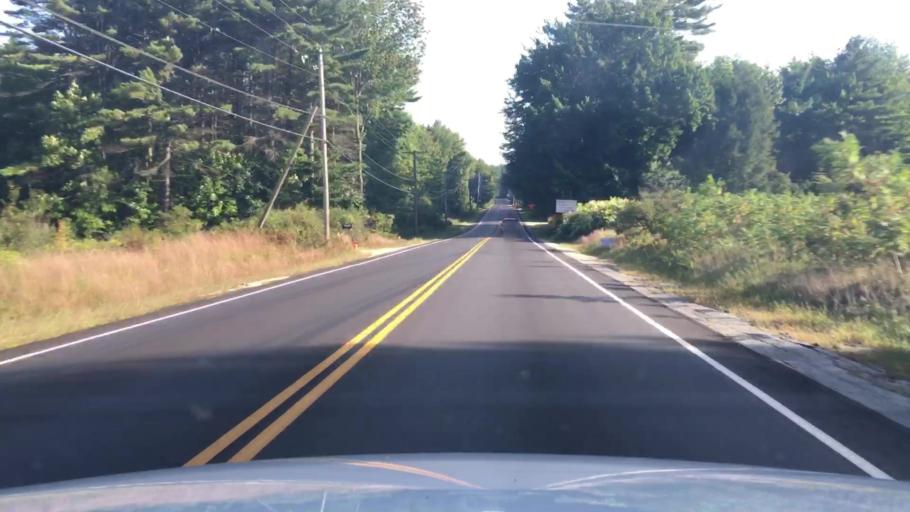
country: US
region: Maine
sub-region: Cumberland County
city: Cumberland Center
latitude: 43.8399
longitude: -70.3216
